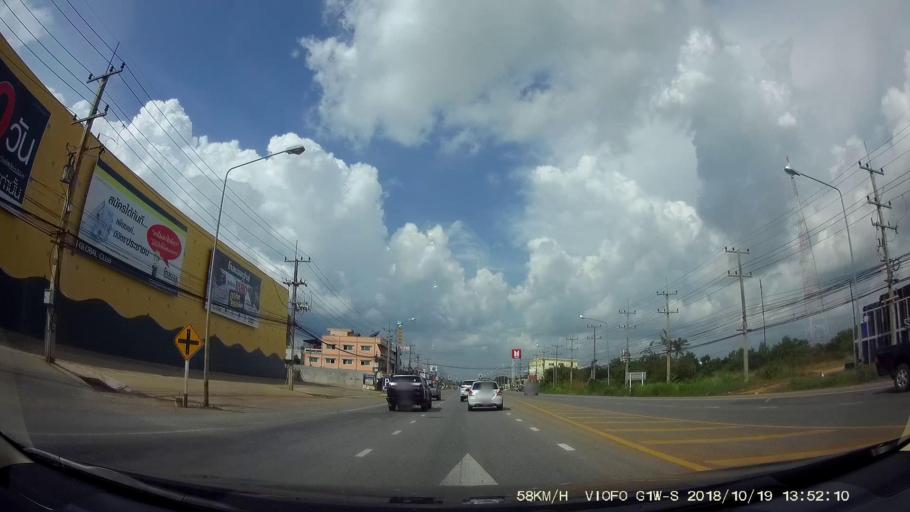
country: TH
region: Chaiyaphum
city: Chaiyaphum
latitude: 15.7642
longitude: 102.0249
